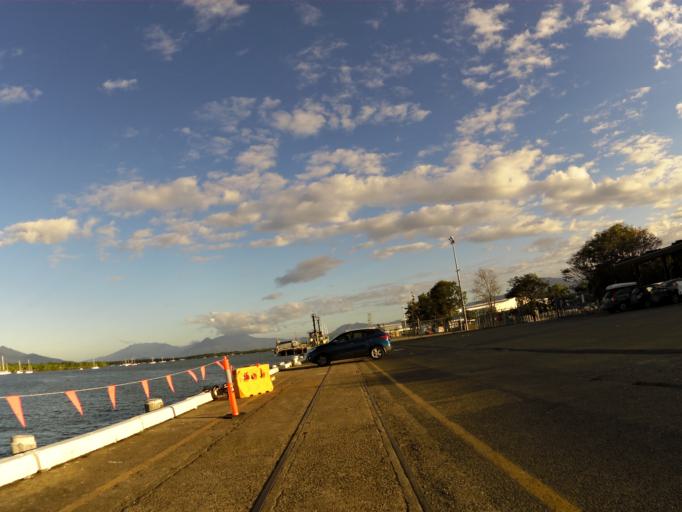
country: AU
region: Queensland
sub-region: Cairns
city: Cairns
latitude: -16.9274
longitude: 145.7803
